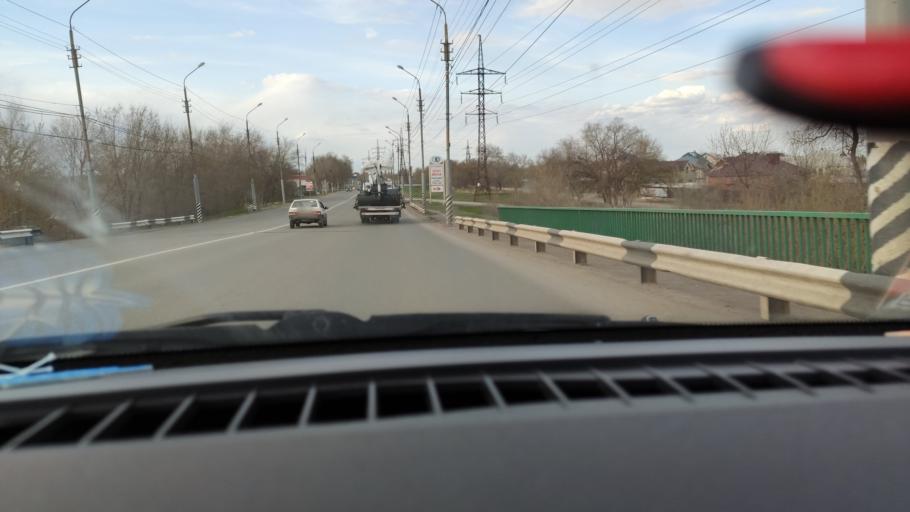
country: RU
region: Saratov
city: Privolzhskiy
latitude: 51.4208
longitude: 46.0472
